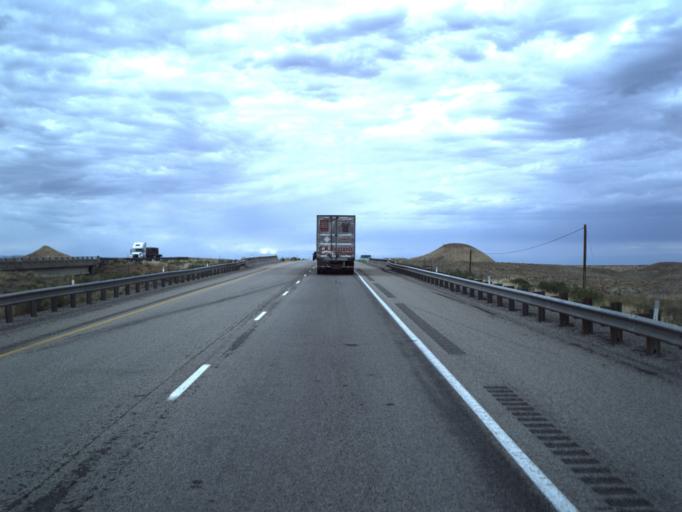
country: US
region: Utah
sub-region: Grand County
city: Moab
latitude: 38.9461
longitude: -109.3968
